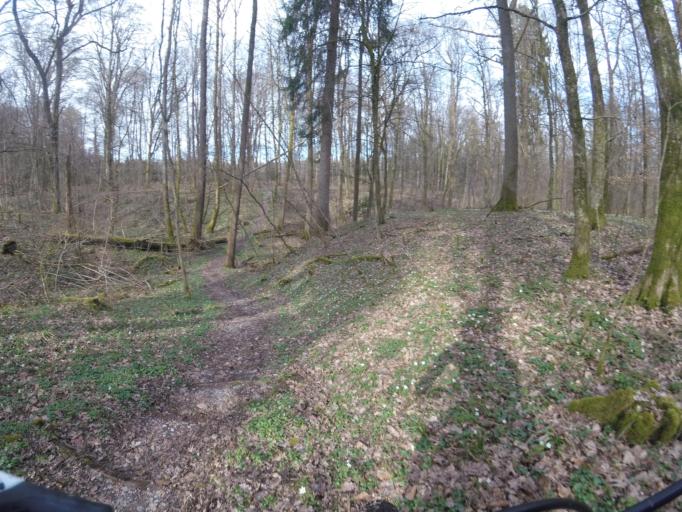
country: DE
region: Baden-Wuerttemberg
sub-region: Regierungsbezirk Stuttgart
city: Backnang
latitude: 48.9628
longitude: 9.4480
